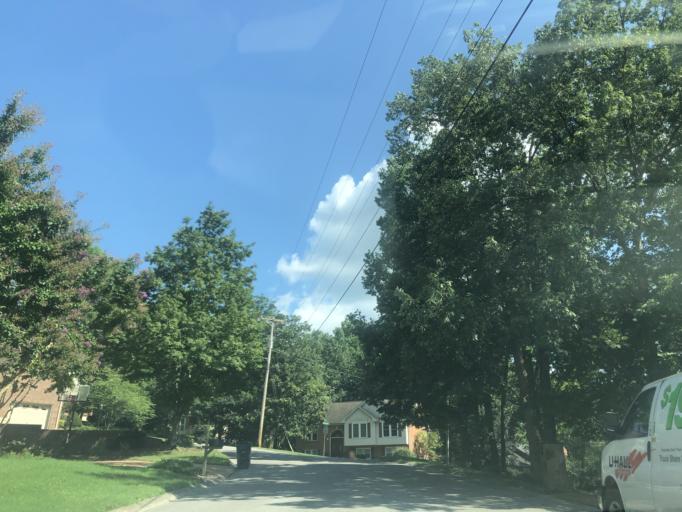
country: US
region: Tennessee
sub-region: Wilson County
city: Green Hill
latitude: 36.1926
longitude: -86.5998
